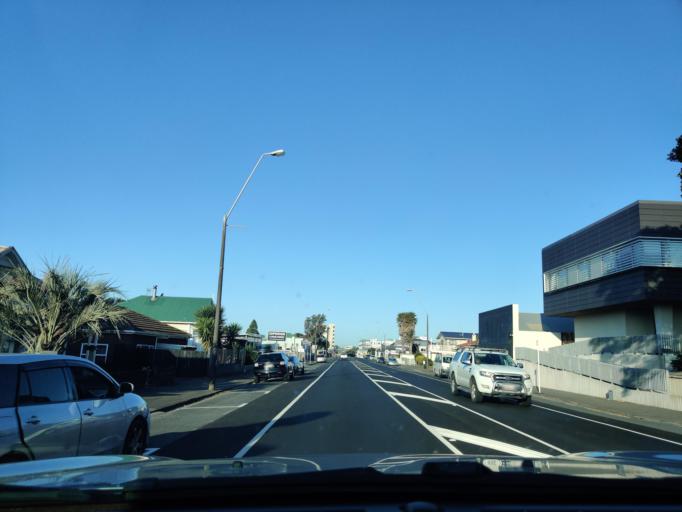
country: NZ
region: Taranaki
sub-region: New Plymouth District
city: New Plymouth
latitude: -39.0582
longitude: 174.0634
